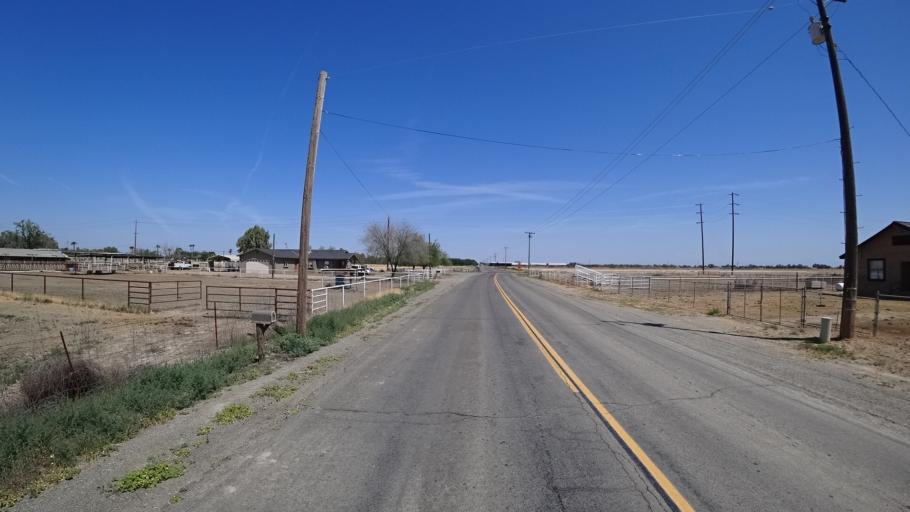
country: US
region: California
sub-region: Kings County
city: Stratford
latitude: 36.2395
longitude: -119.7986
